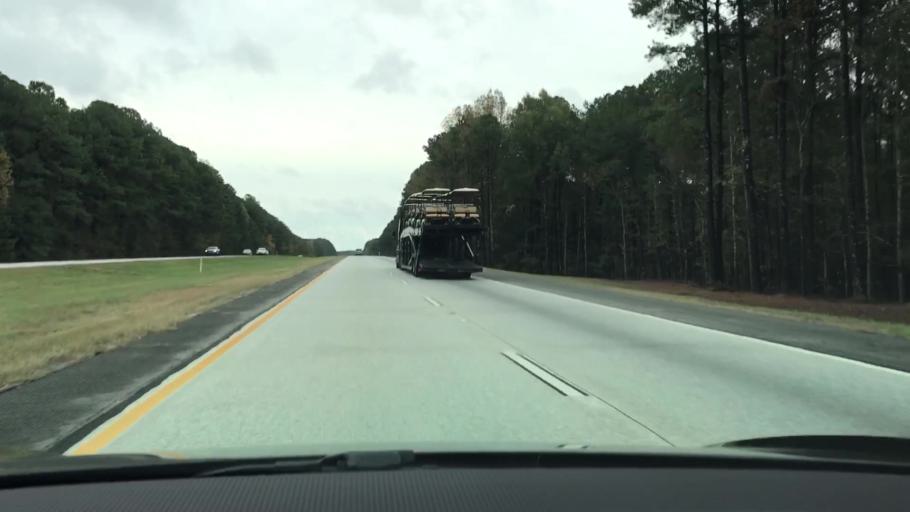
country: US
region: Georgia
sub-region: Taliaferro County
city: Crawfordville
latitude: 33.5071
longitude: -82.8368
